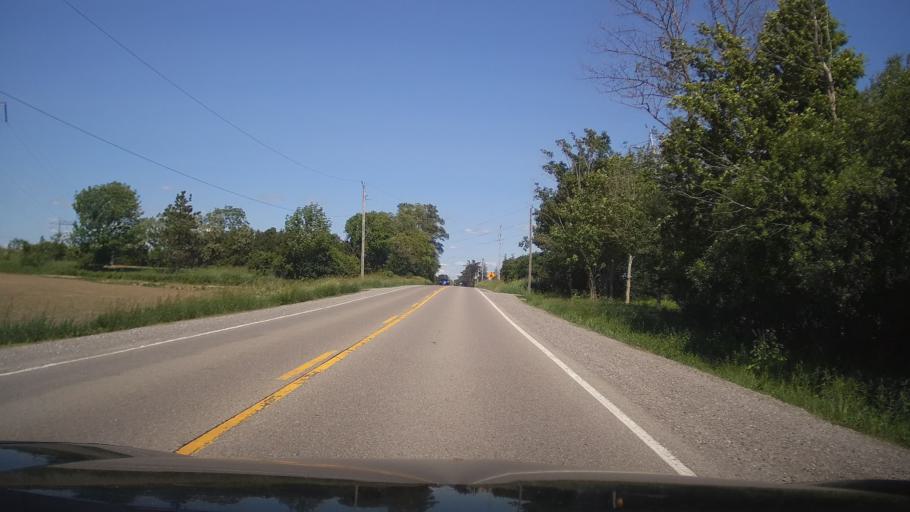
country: CA
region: Ontario
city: Oshawa
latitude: 44.0003
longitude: -78.8346
